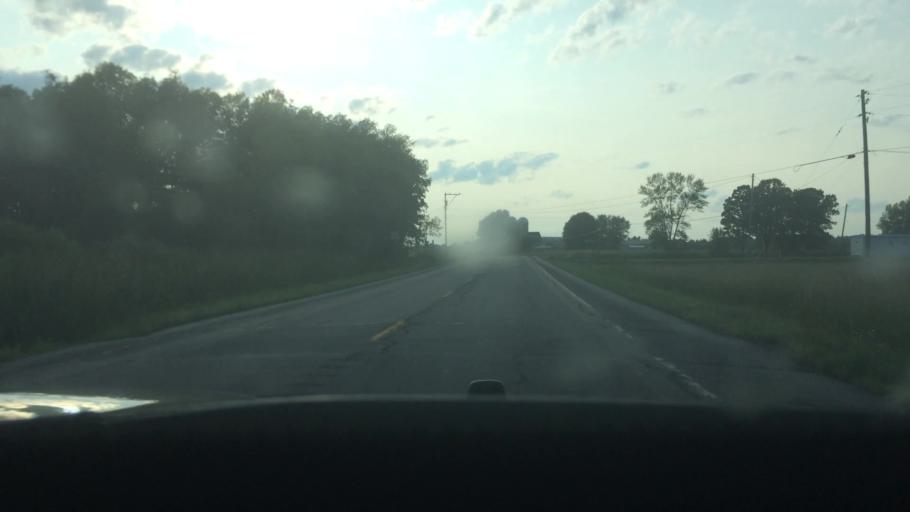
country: US
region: New York
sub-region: St. Lawrence County
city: Ogdensburg
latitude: 44.6742
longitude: -75.4005
